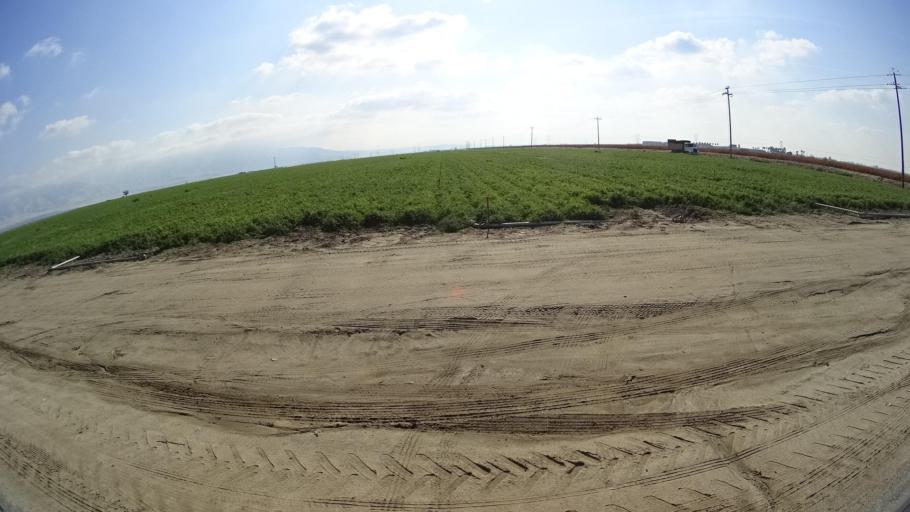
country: US
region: California
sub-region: Kern County
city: Arvin
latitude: 35.2674
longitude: -118.8244
